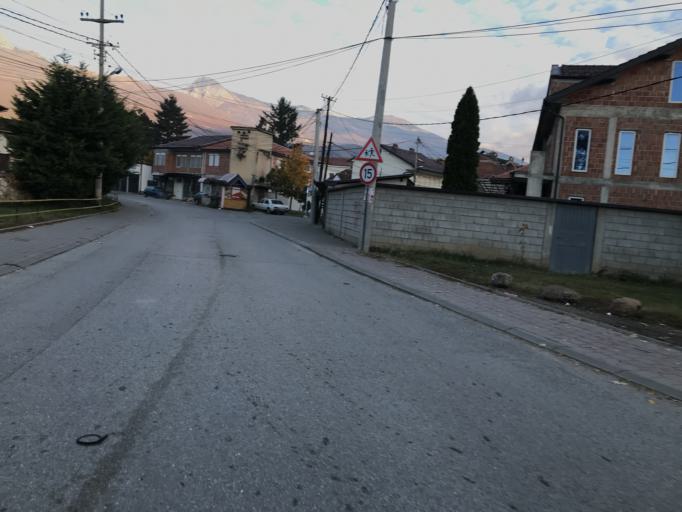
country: XK
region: Pec
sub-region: Komuna e Pejes
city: Peje
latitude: 42.6582
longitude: 20.3015
